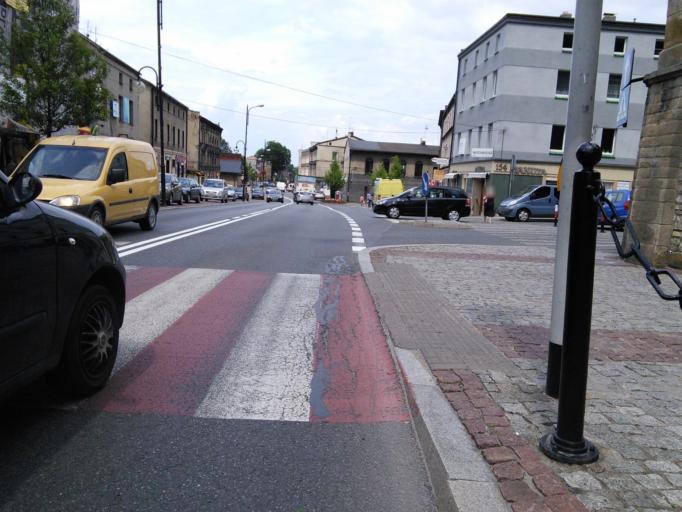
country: PL
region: Silesian Voivodeship
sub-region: Piekary Slaskie
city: Piekary Slaskie
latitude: 50.3840
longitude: 18.9441
